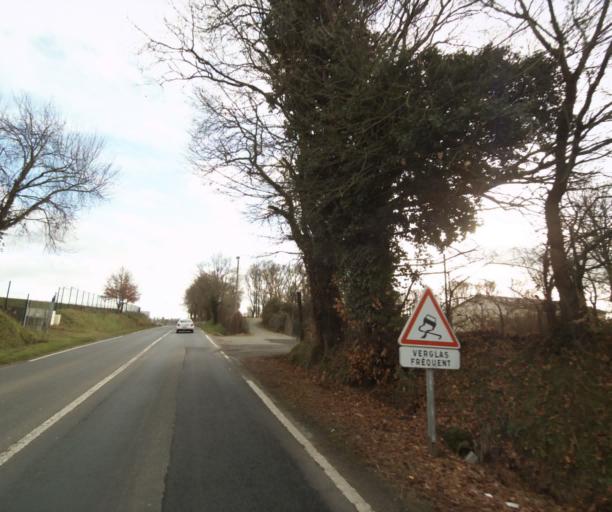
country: FR
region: Pays de la Loire
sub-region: Departement de la Sarthe
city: Arnage
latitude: 47.9348
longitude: 0.2079
